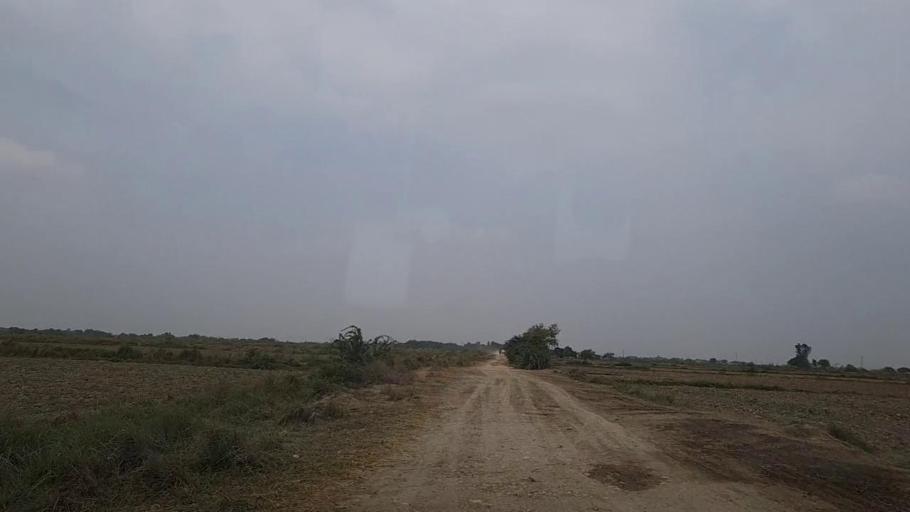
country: PK
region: Sindh
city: Mirpur Sakro
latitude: 24.5981
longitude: 67.6974
